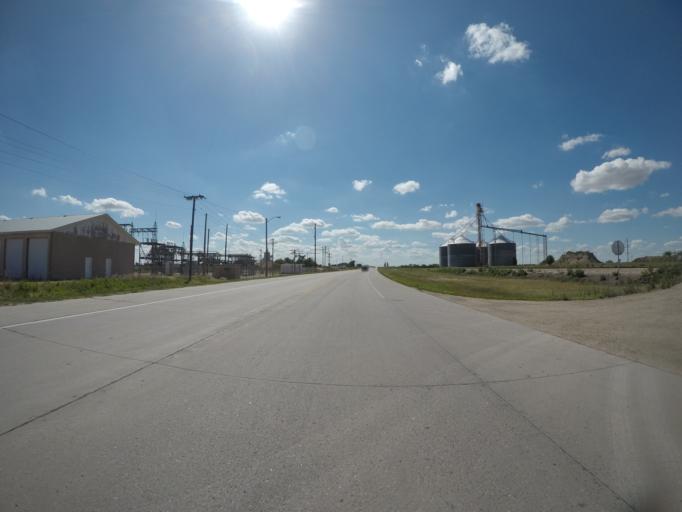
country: US
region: Colorado
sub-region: Phillips County
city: Holyoke
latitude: 40.5852
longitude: -102.3105
